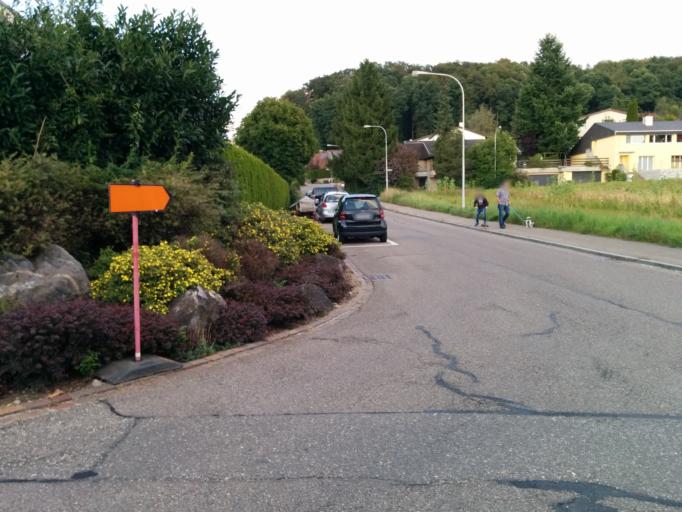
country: CH
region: Zurich
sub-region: Bezirk Buelach
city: Buelach / Soligaenter
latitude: 47.5289
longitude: 8.5443
